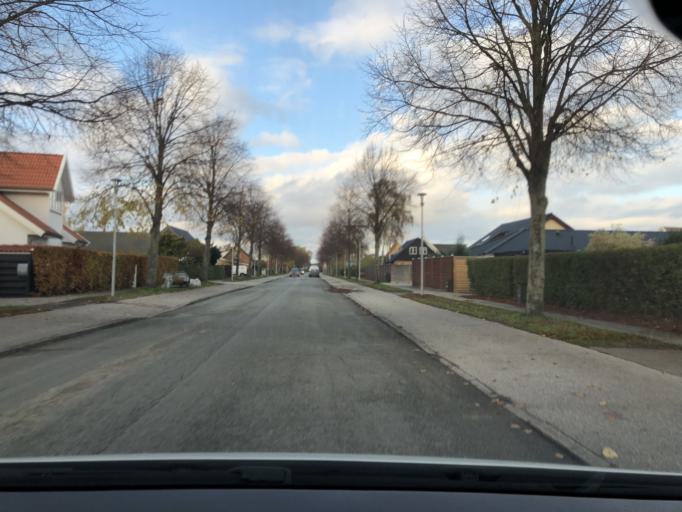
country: DK
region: Capital Region
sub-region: Tarnby Kommune
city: Tarnby
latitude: 55.6184
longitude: 12.5979
